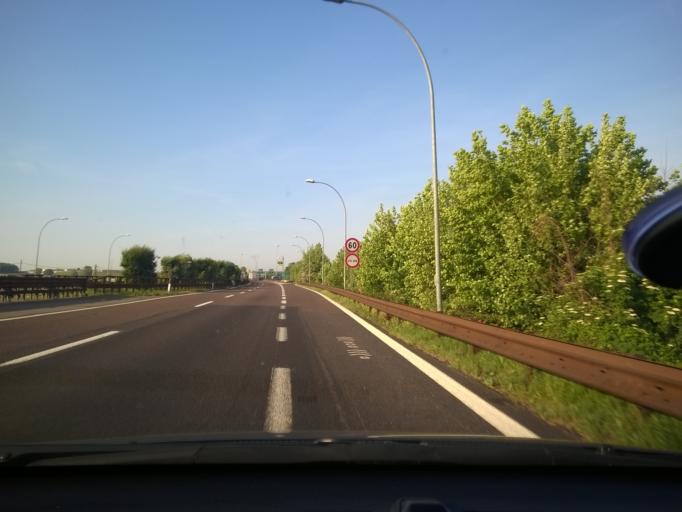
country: IT
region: Lombardy
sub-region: Provincia di Mantova
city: San Biagio
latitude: 45.0639
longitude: 10.8421
